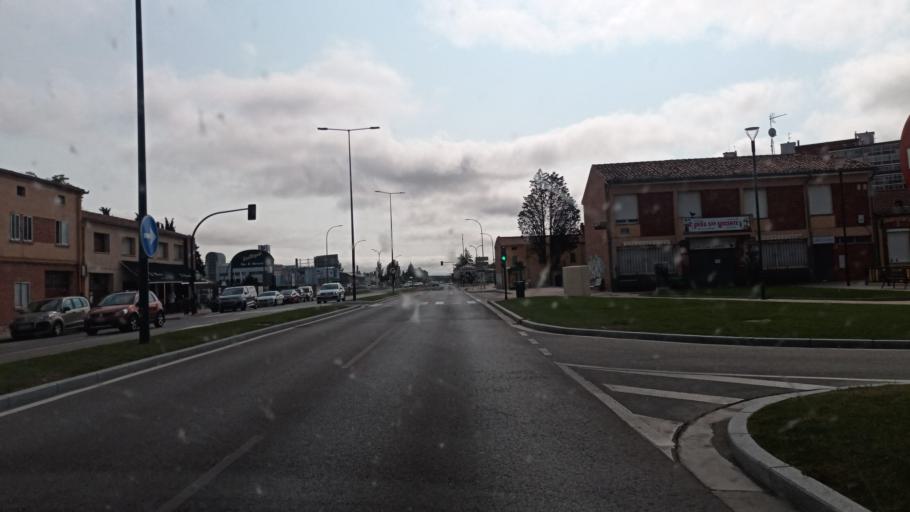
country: ES
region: Castille and Leon
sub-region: Provincia de Burgos
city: Burgos
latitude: 42.3450
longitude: -3.6511
